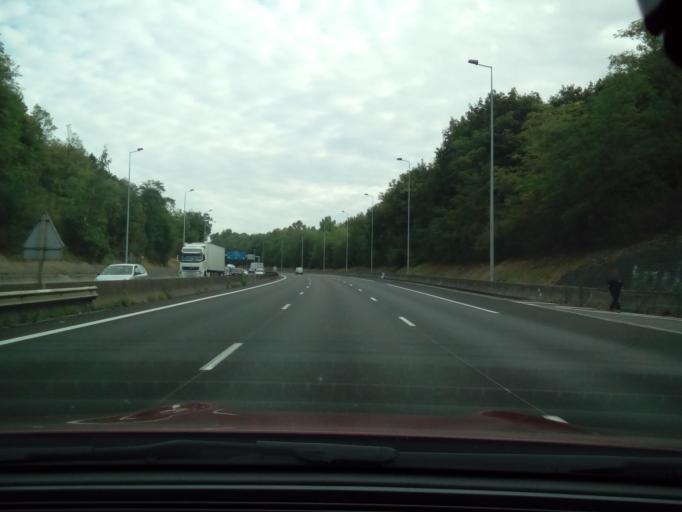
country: FR
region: Rhone-Alpes
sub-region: Departement du Rhone
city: Rillieux-la-Pape
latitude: 45.8159
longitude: 4.9175
